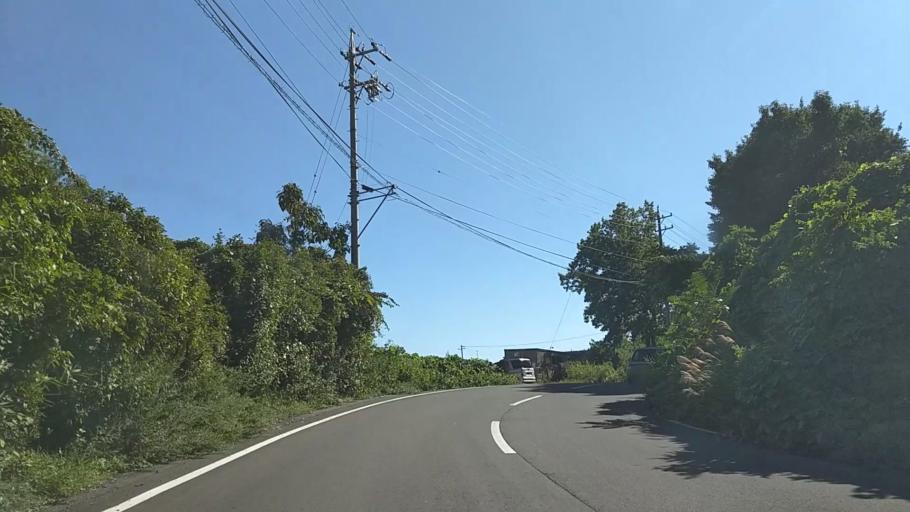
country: JP
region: Nagano
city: Nagano-shi
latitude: 36.5801
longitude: 138.1203
